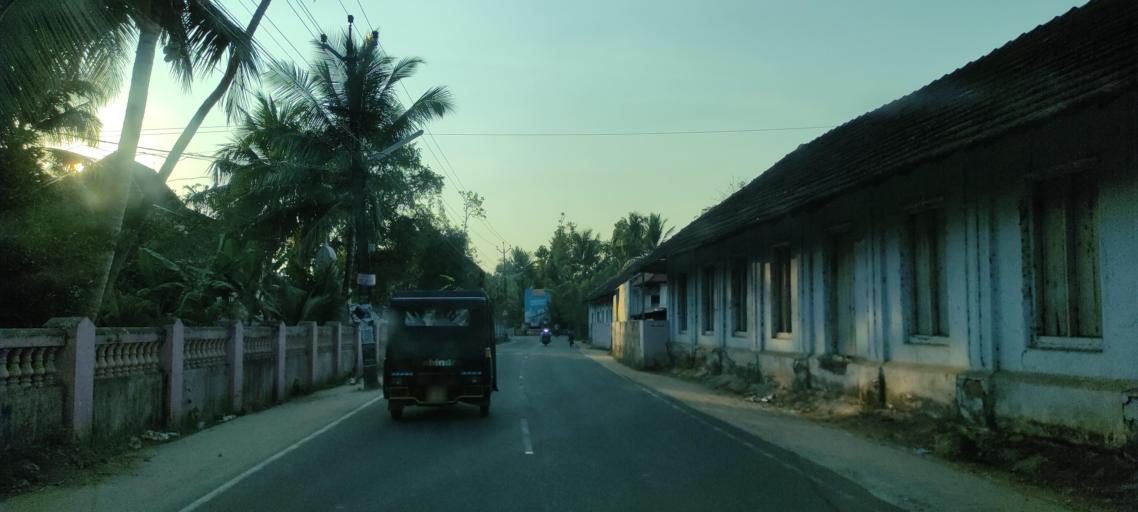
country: IN
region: Kerala
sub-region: Alappuzha
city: Kutiatodu
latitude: 9.7747
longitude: 76.3391
